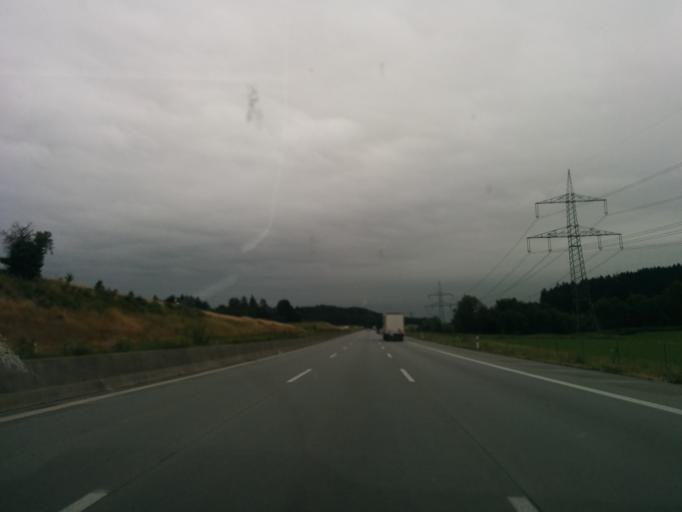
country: DE
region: Bavaria
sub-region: Swabia
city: Dasing
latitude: 48.4002
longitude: 11.0045
